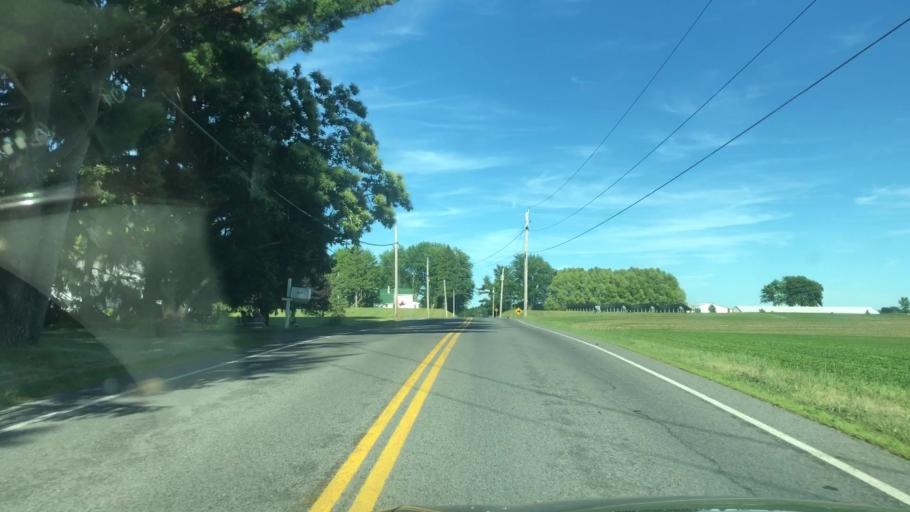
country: US
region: New York
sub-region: Wayne County
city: Macedon
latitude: 43.1163
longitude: -77.3184
